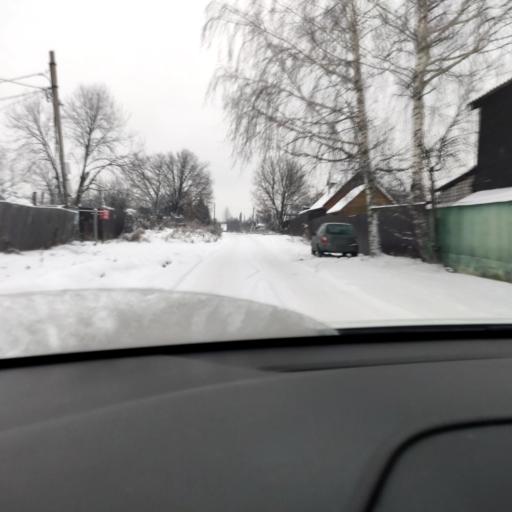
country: RU
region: Tatarstan
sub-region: Gorod Kazan'
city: Kazan
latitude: 55.8394
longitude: 49.2177
